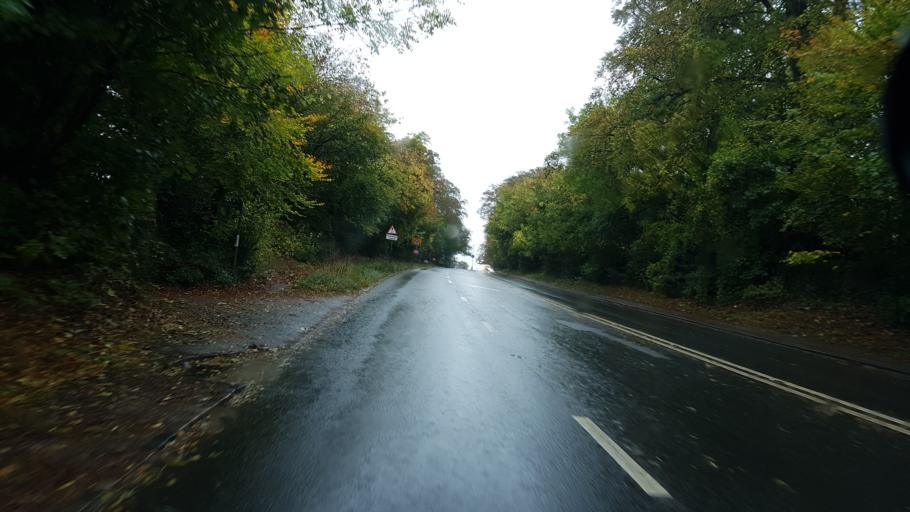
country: GB
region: England
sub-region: Gloucestershire
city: Stow on the Wold
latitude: 51.9237
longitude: -1.7257
